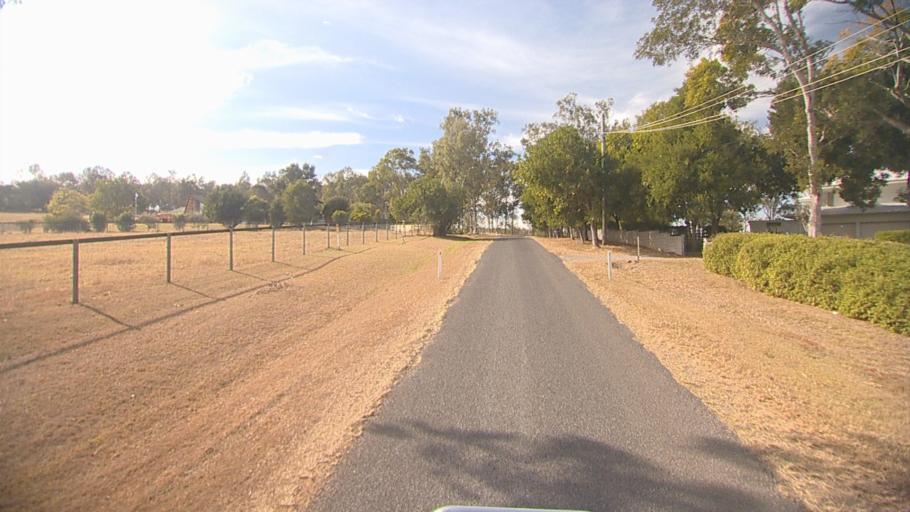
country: AU
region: Queensland
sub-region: Logan
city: Cedar Vale
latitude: -27.9090
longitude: 152.9846
